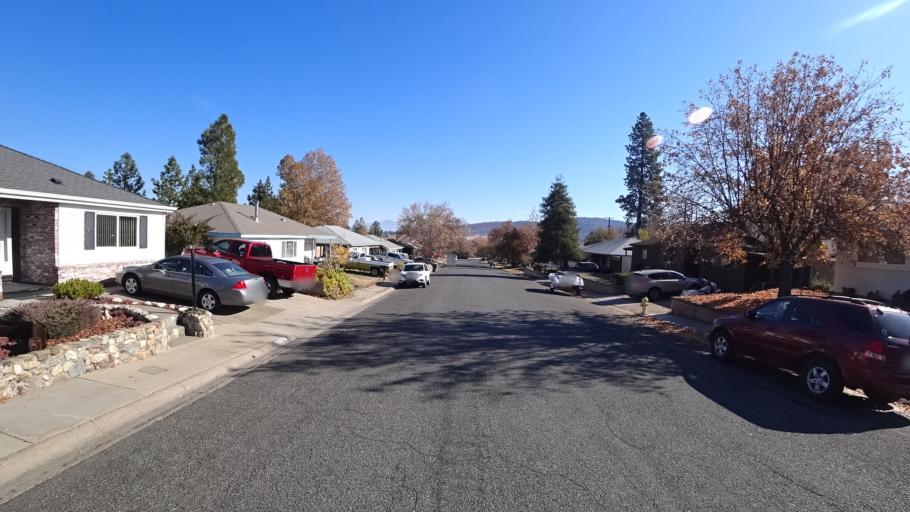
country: US
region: California
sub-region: Siskiyou County
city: Yreka
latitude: 41.7404
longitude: -122.6415
